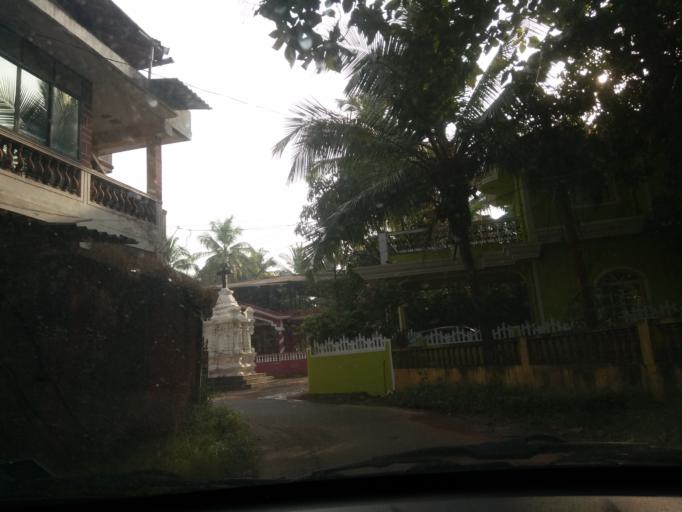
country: IN
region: Goa
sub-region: South Goa
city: Chinchinim
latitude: 15.2112
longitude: 73.9810
